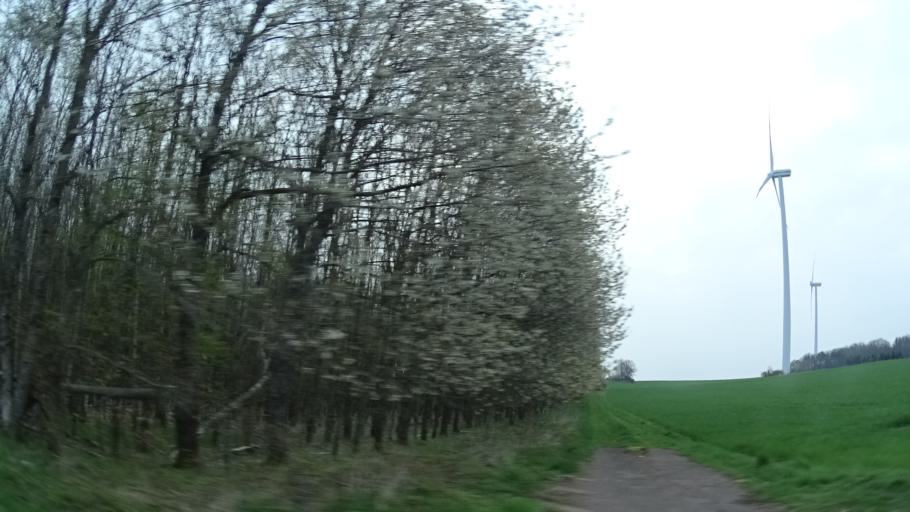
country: DE
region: Rheinland-Pfalz
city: Rimsberg
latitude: 49.6424
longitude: 7.2067
